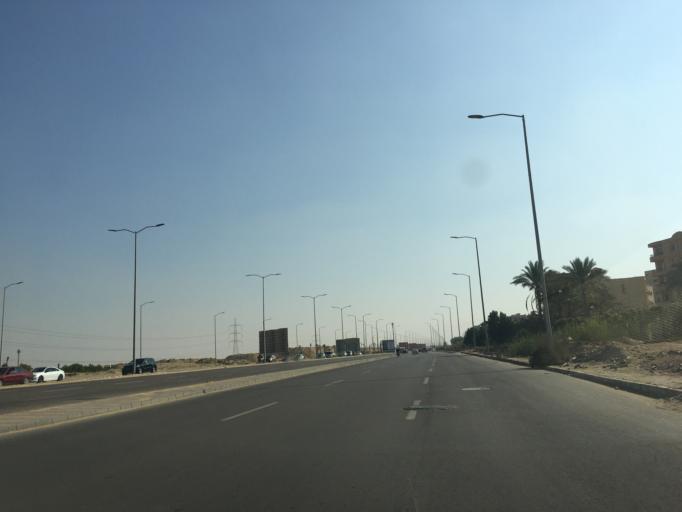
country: EG
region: Al Jizah
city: Awsim
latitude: 30.0047
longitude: 30.9848
